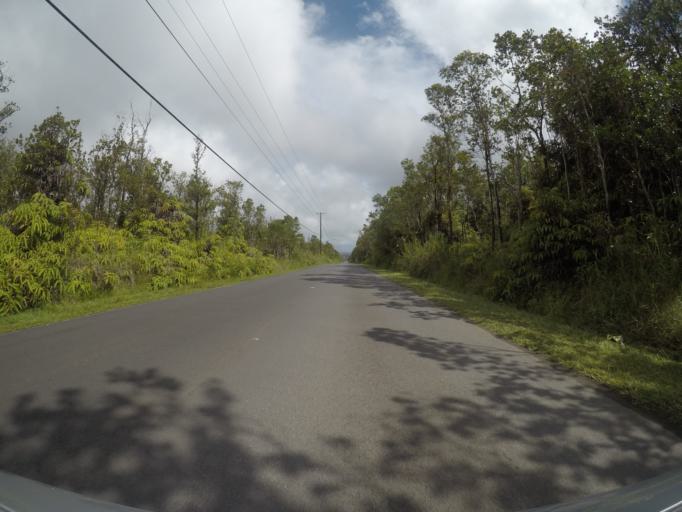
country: US
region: Hawaii
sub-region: Hawaii County
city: Fern Acres
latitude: 19.4639
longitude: -155.1333
